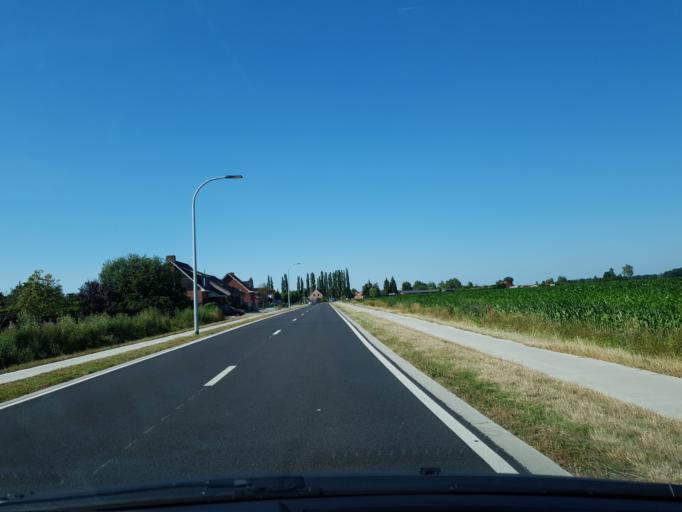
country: BE
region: Flanders
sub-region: Provincie Antwerpen
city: Beerse
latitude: 51.3326
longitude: 4.8556
